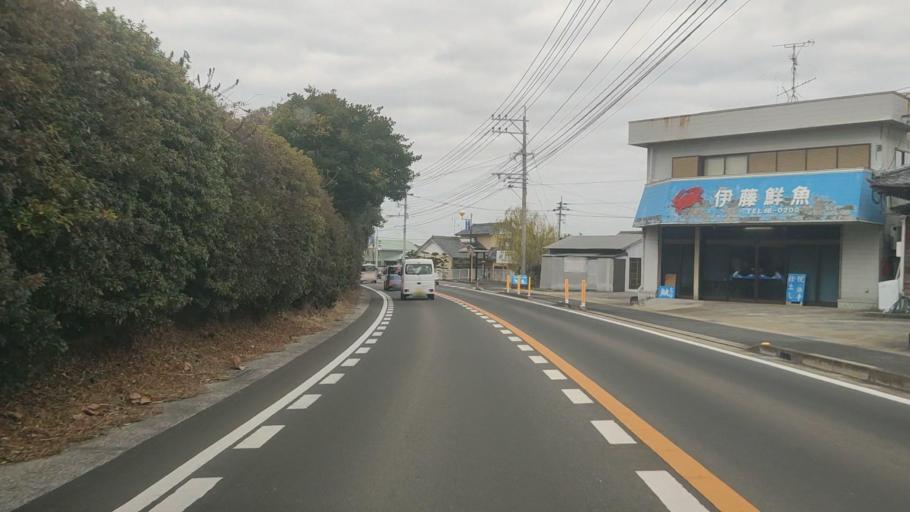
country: JP
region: Nagasaki
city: Shimabara
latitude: 32.8546
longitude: 130.3382
